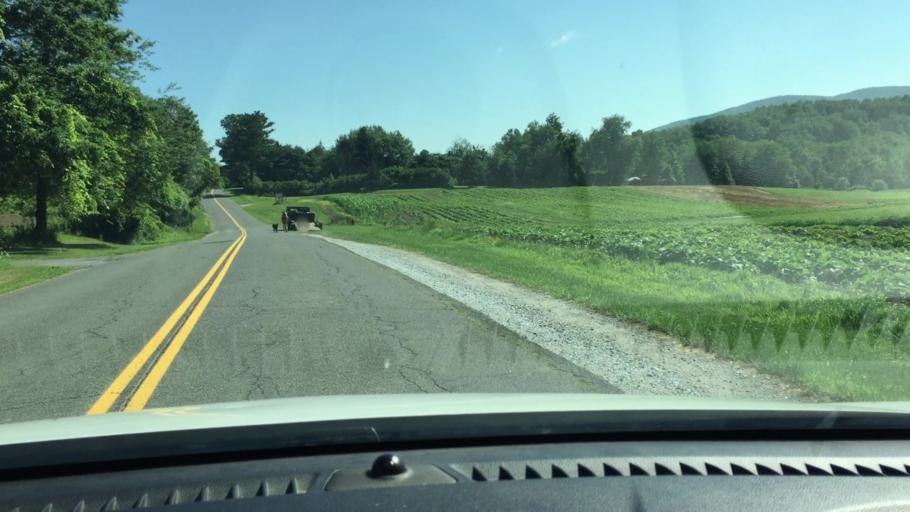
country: US
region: Massachusetts
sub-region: Berkshire County
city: Lanesborough
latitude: 42.5135
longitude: -73.2176
